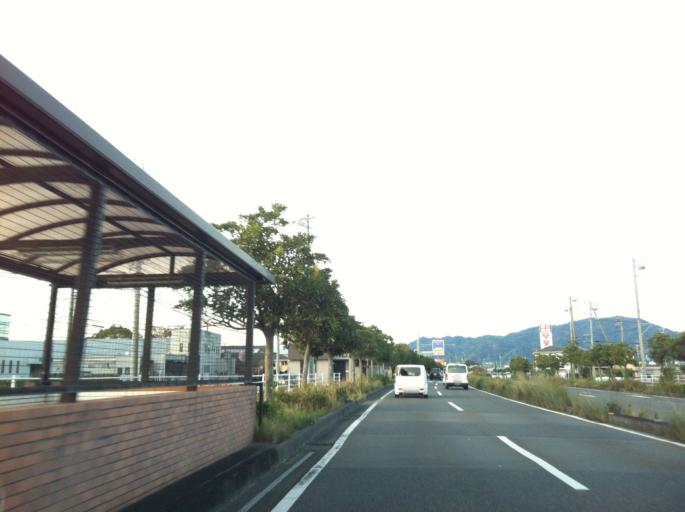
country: JP
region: Shizuoka
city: Yaizu
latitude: 34.8516
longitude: 138.2994
